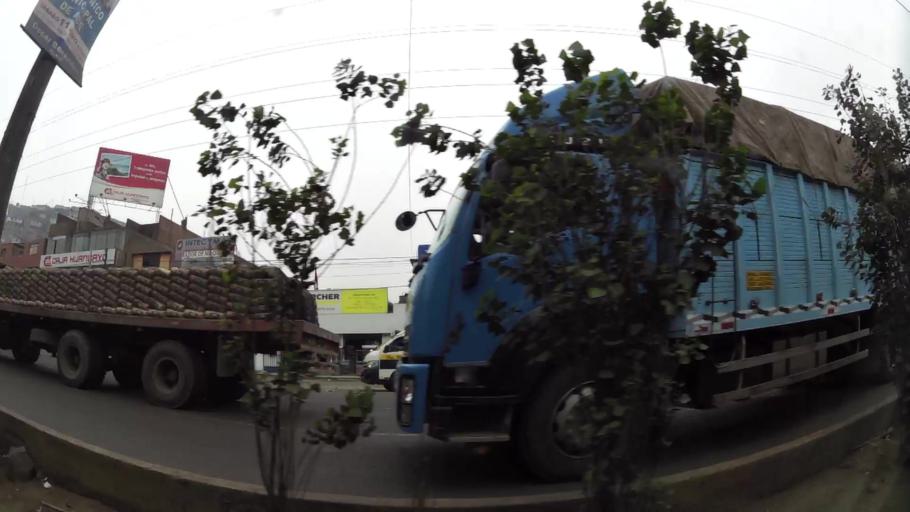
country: PE
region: Lima
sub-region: Lima
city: Vitarte
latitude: -12.0276
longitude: -76.9227
